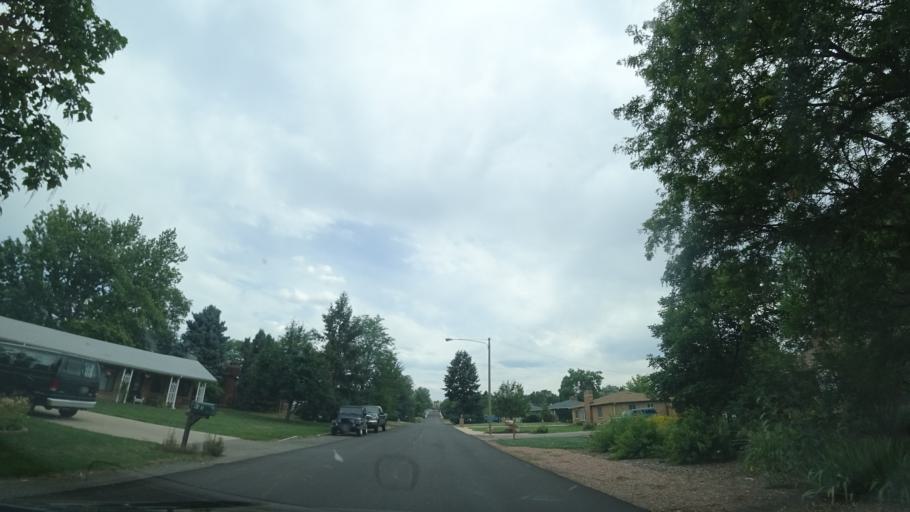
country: US
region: Colorado
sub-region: Jefferson County
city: Lakewood
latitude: 39.7165
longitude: -105.0862
